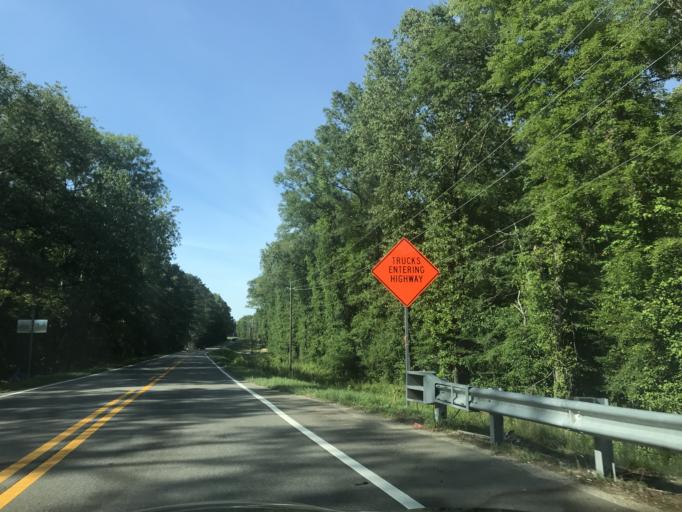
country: US
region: North Carolina
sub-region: Johnston County
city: Clayton
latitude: 35.6004
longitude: -78.5354
